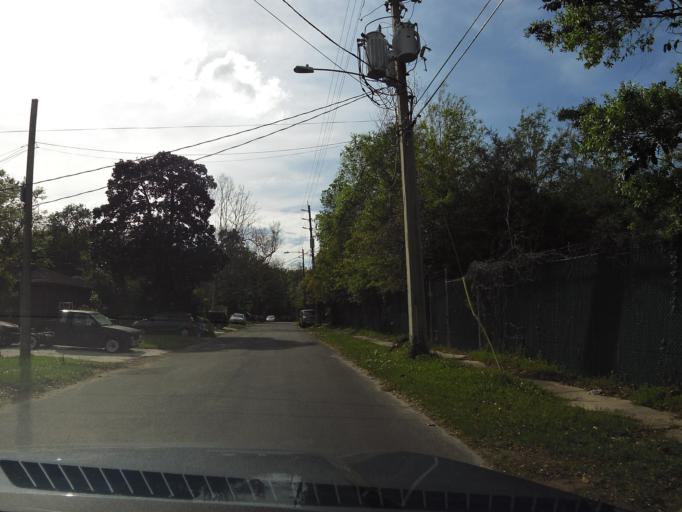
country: US
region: Florida
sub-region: Duval County
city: Jacksonville
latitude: 30.3183
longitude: -81.7183
